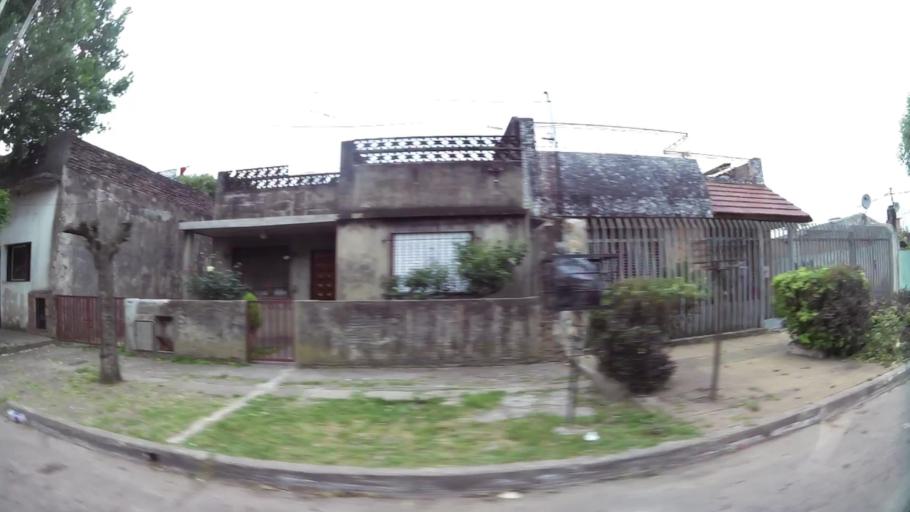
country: AR
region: Buenos Aires
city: San Justo
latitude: -34.6980
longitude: -58.5654
